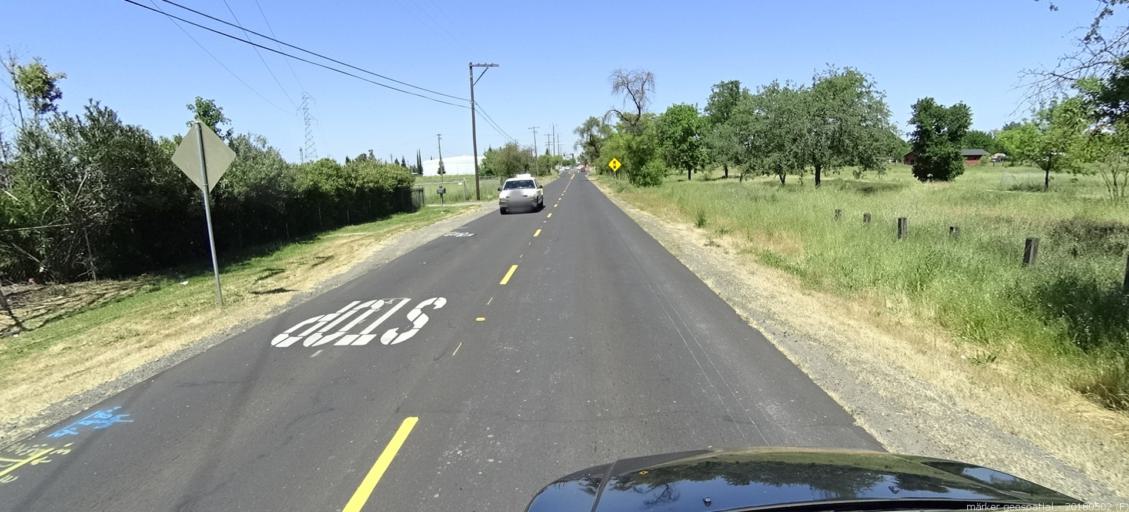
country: US
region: California
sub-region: Sacramento County
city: Rio Linda
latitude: 38.6454
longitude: -121.4478
